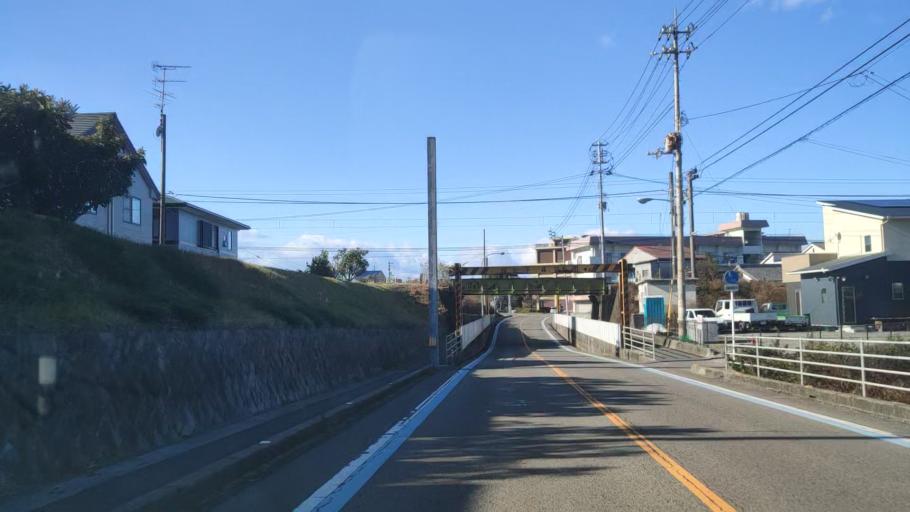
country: JP
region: Ehime
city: Saijo
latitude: 33.9090
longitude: 133.1828
